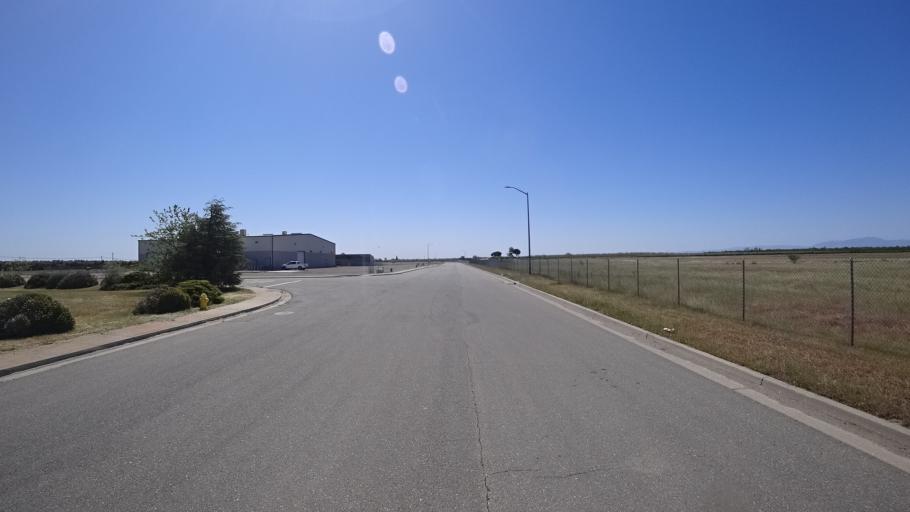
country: US
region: California
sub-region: Glenn County
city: Orland
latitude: 39.7182
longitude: -122.1433
